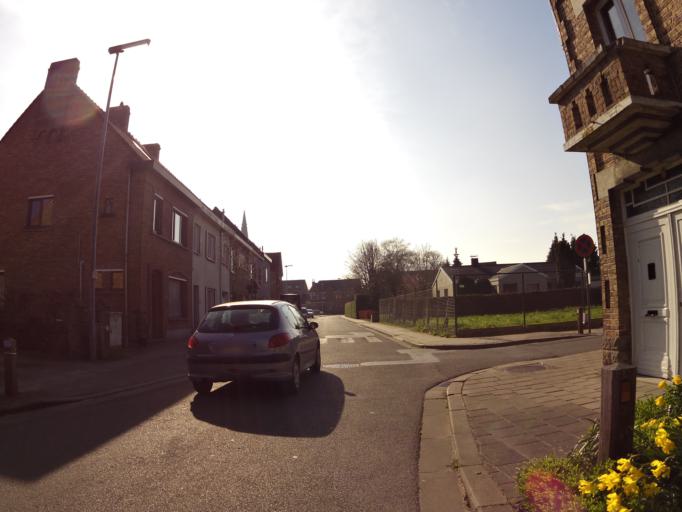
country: BE
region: Flanders
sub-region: Provincie West-Vlaanderen
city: Gistel
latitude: 51.1588
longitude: 2.9708
